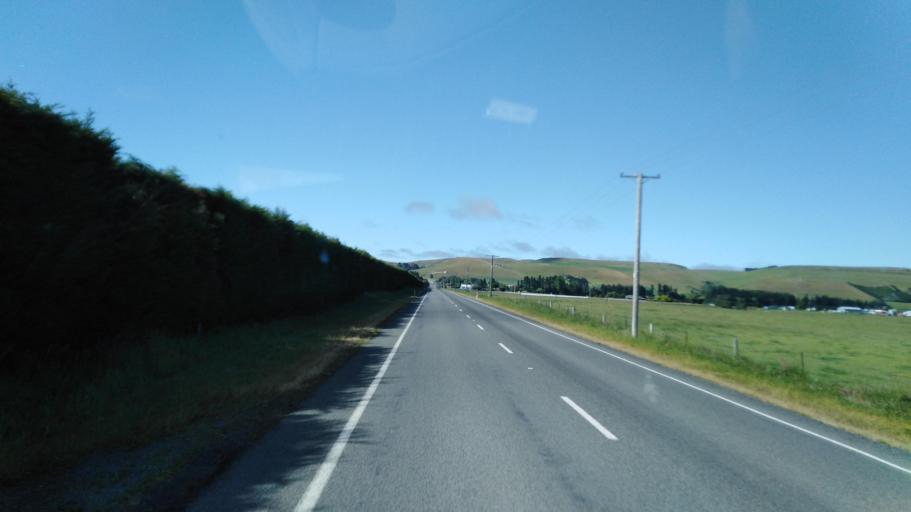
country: NZ
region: Canterbury
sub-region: Hurunui District
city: Amberley
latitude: -42.9578
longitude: 172.7088
